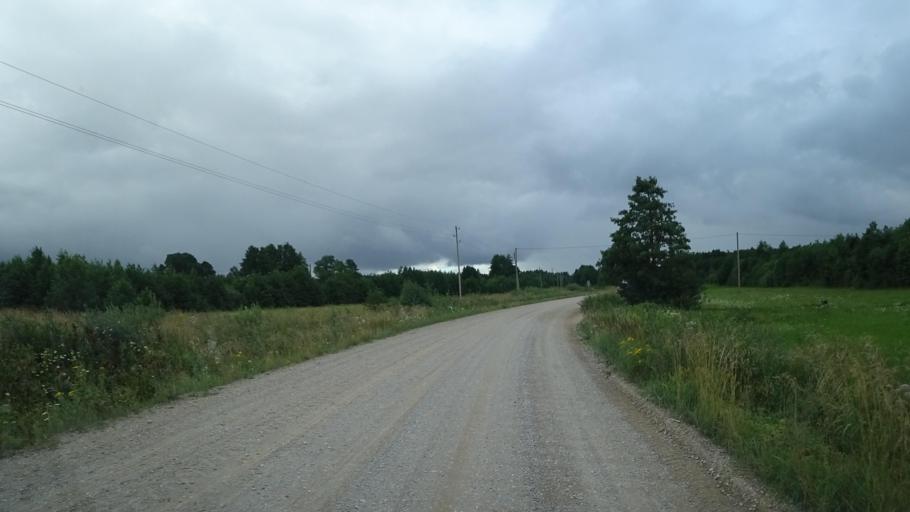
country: LV
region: Liepaja
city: Vec-Liepaja
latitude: 56.6291
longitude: 21.0493
